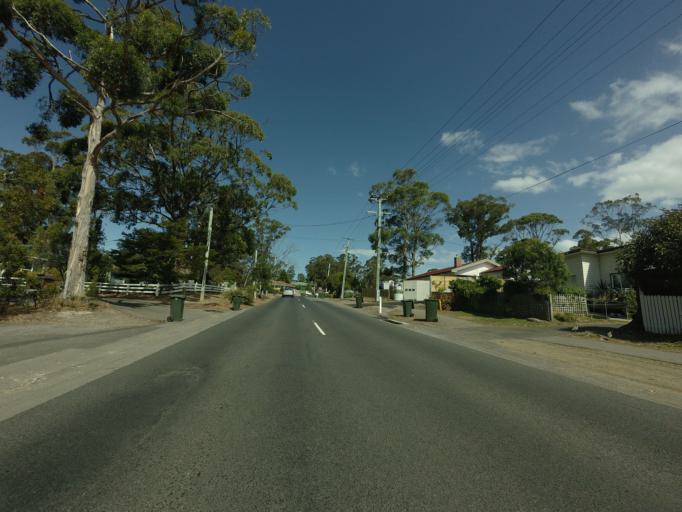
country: AU
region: Tasmania
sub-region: Hobart
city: Dynnyrne
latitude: -42.9214
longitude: 147.3235
